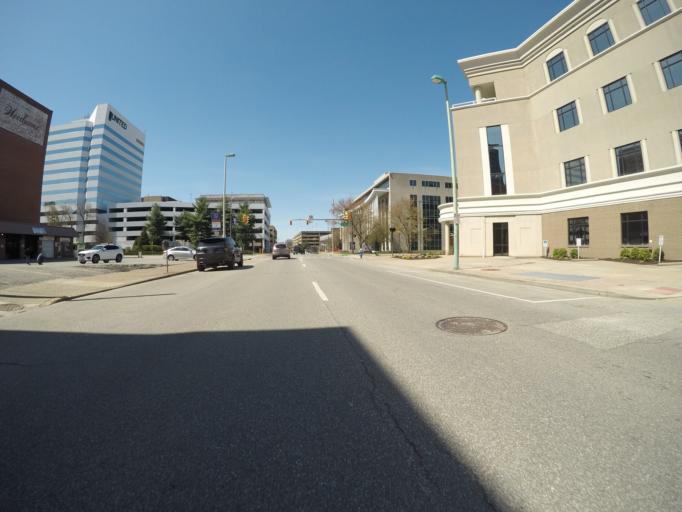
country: US
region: West Virginia
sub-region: Kanawha County
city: Charleston
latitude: 38.3510
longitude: -81.6363
